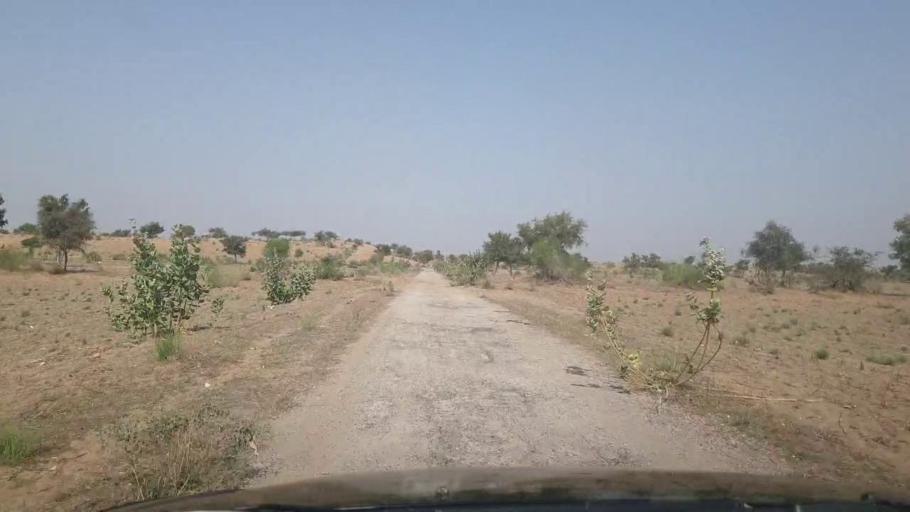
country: PK
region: Sindh
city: Islamkot
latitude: 25.0629
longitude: 70.2049
